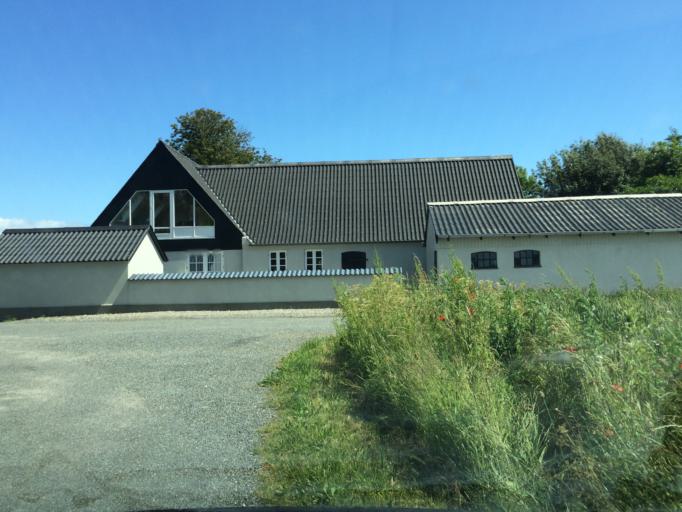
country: DK
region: Central Jutland
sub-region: Samso Kommune
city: Tranebjerg
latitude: 55.8361
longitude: 10.5319
